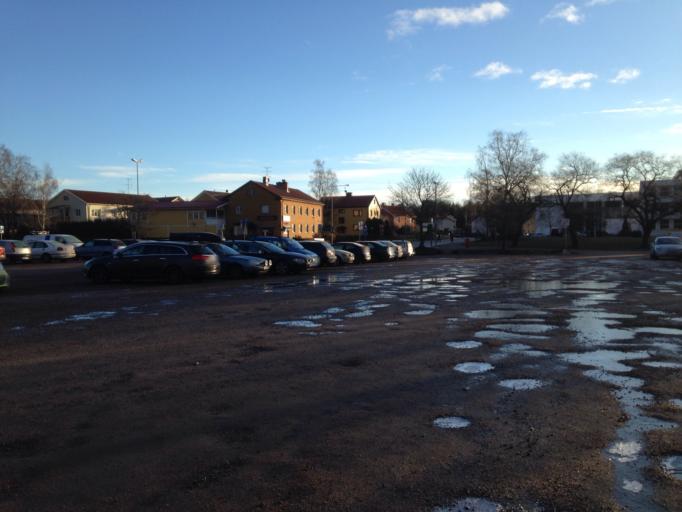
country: SE
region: Vaestmanland
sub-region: Vasteras
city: Vasteras
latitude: 59.6211
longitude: 16.5352
